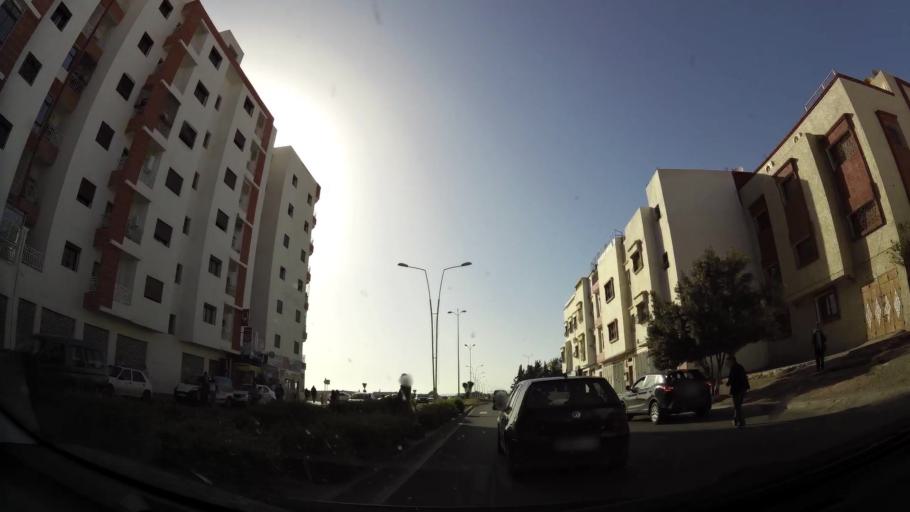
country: MA
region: Oued ed Dahab-Lagouira
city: Dakhla
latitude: 30.4006
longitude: -9.5541
